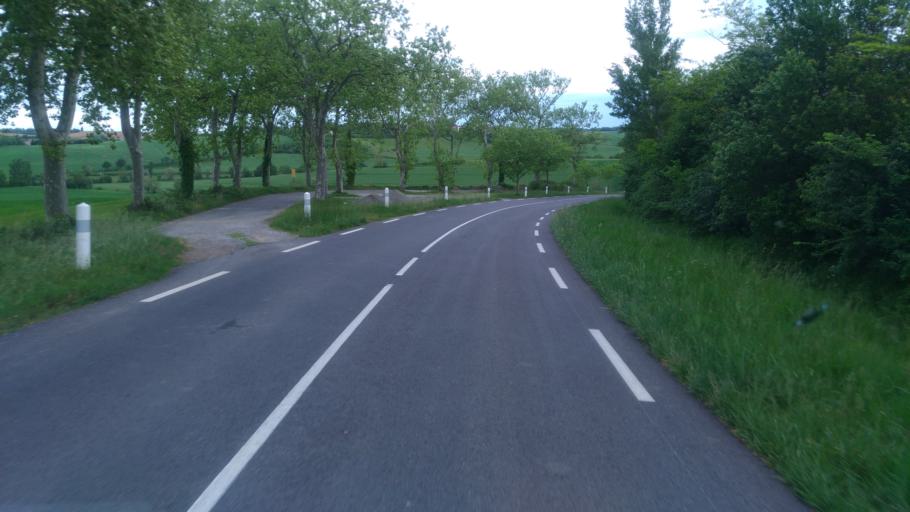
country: FR
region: Midi-Pyrenees
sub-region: Departement de la Haute-Garonne
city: Avignonet-Lauragais
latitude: 43.4411
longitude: 1.7826
